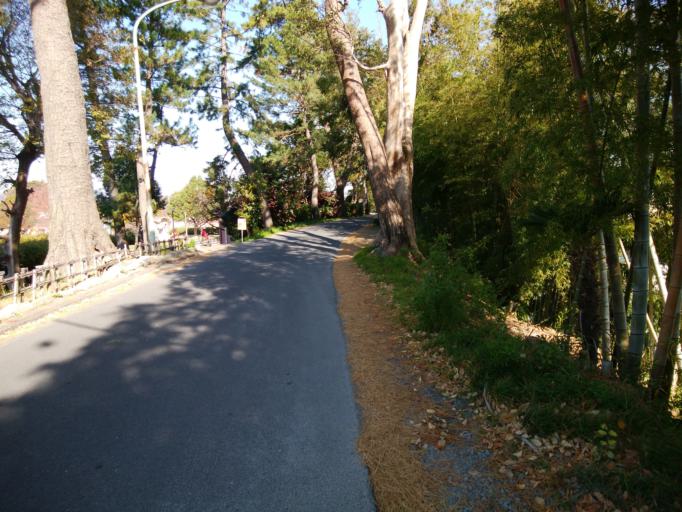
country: JP
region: Aichi
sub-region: Tsushima-shi
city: Tsushima
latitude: 35.1720
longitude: 136.7210
